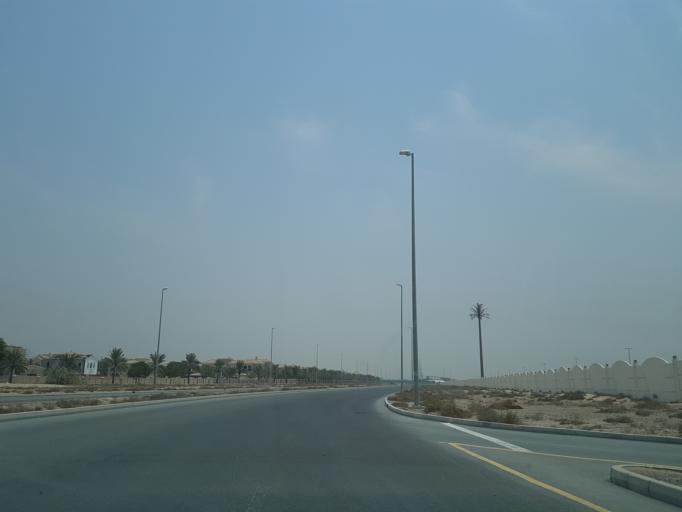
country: AE
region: Dubai
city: Dubai
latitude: 25.0368
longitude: 55.2464
